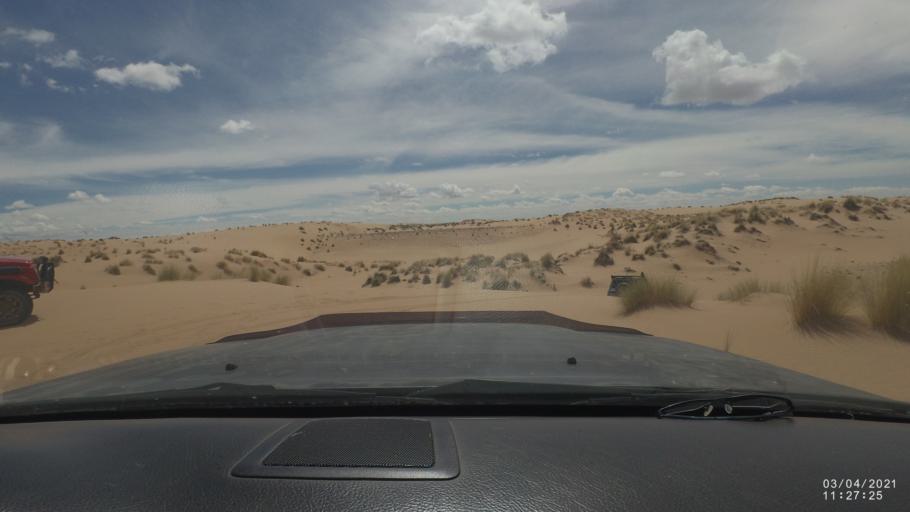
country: BO
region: Oruro
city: Poopo
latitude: -18.7028
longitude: -67.5112
